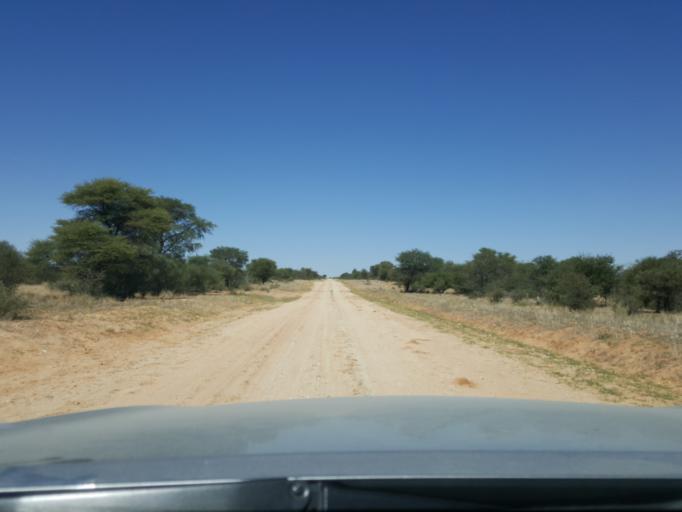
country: BW
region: Kgalagadi
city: Hukuntsi
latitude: -24.0940
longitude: 21.2288
